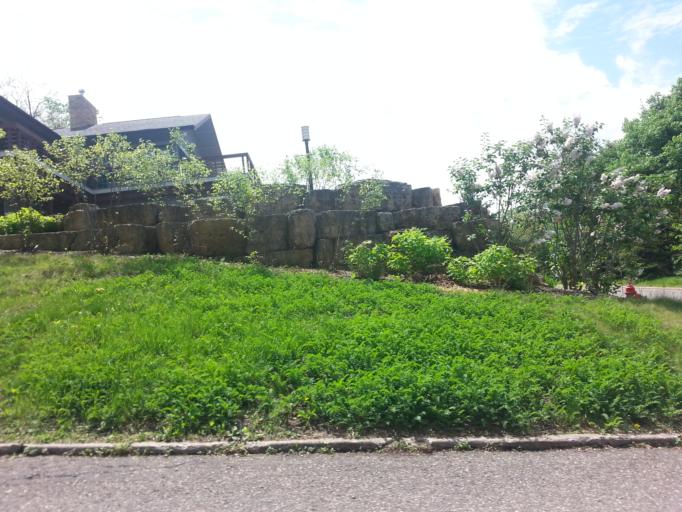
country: US
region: Wisconsin
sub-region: Saint Croix County
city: Hudson
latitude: 44.9804
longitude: -92.7437
